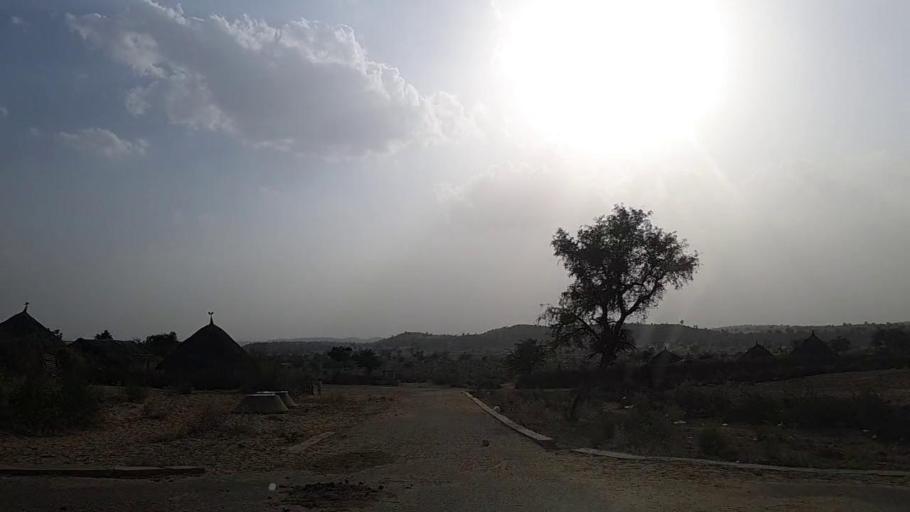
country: PK
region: Sindh
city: Islamkot
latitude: 24.7346
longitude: 70.1585
